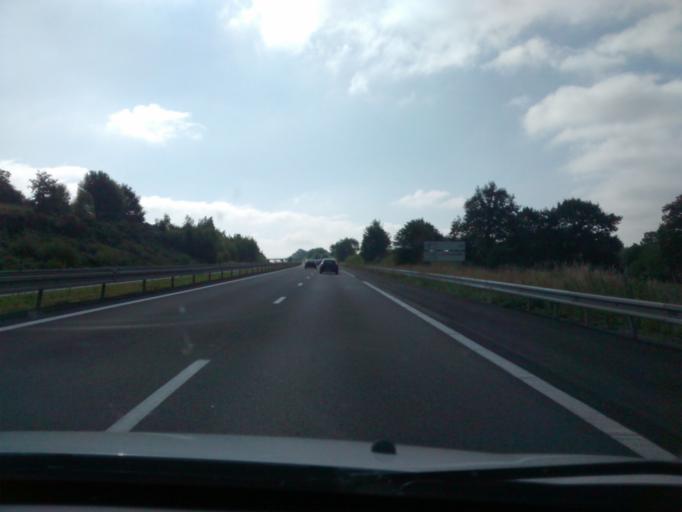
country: FR
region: Pays de la Loire
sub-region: Departement de la Mayenne
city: Vaiges
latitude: 48.0535
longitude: -0.4724
